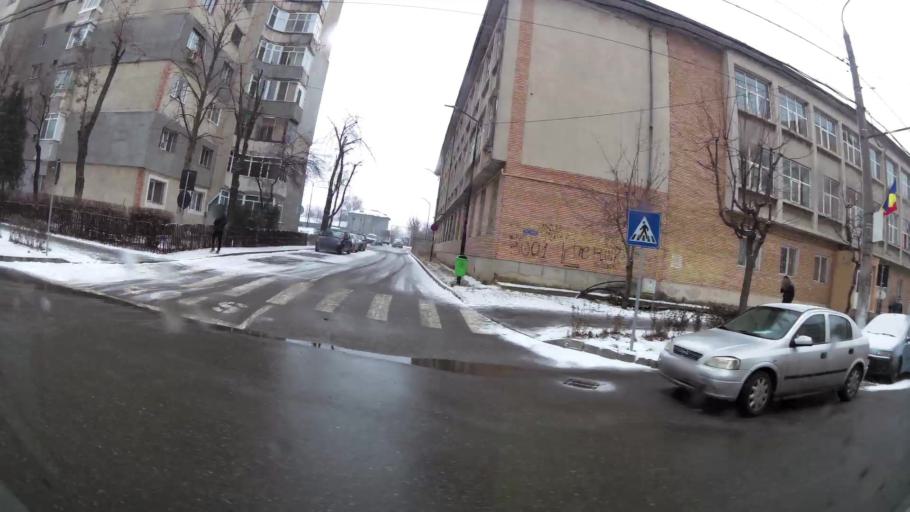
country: RO
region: Dambovita
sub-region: Municipiul Targoviste
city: Targoviste
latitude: 44.9209
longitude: 25.4487
